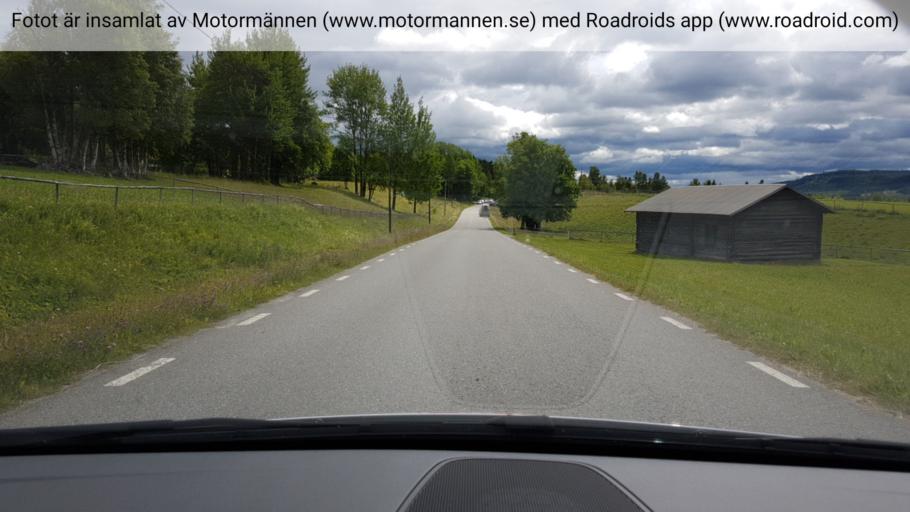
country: SE
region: Jaemtland
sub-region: Bergs Kommun
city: Hoverberg
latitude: 62.5265
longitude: 14.1840
